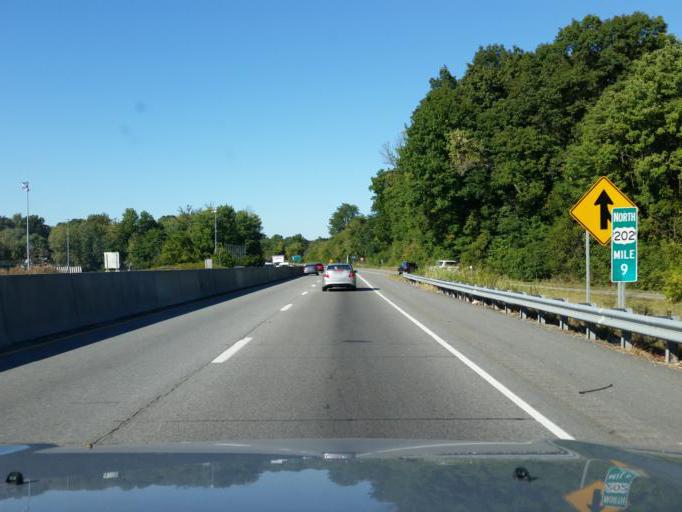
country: US
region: Pennsylvania
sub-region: Chester County
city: West Chester
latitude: 39.9571
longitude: -75.5802
